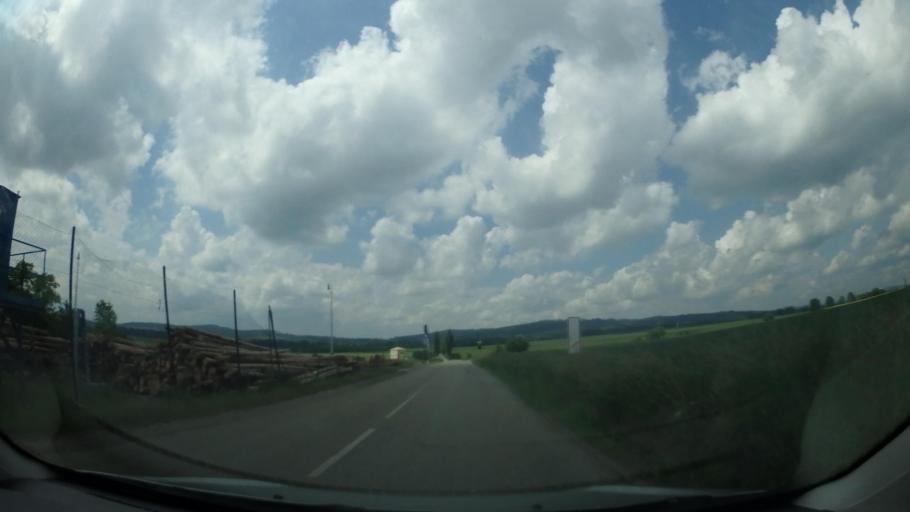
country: CZ
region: South Moravian
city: Velke Opatovice
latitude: 49.5554
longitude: 16.6990
